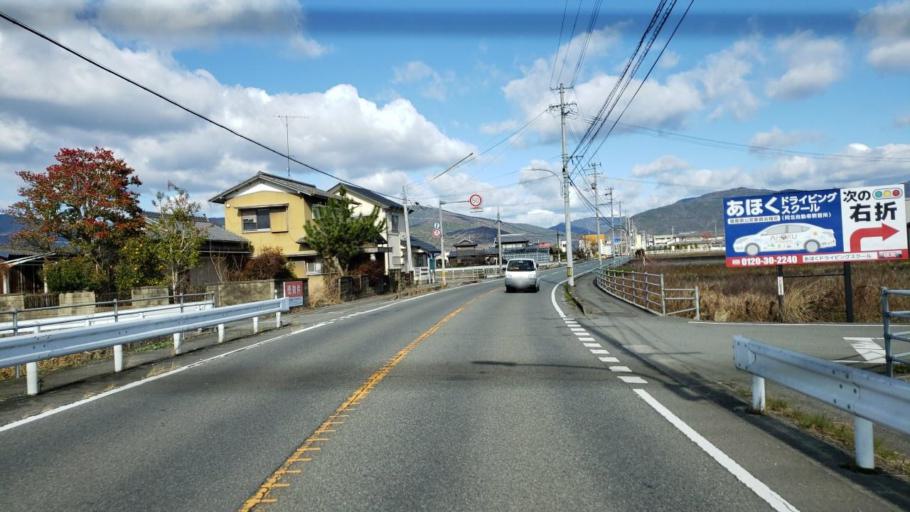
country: JP
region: Tokushima
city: Kamojimacho-jogejima
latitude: 34.0927
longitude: 134.3433
